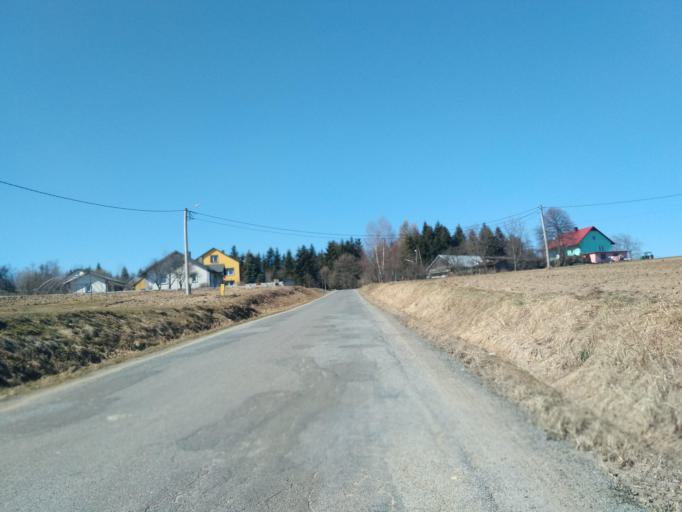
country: PL
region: Subcarpathian Voivodeship
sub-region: Powiat debicki
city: Brzostek
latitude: 49.9567
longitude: 21.4285
